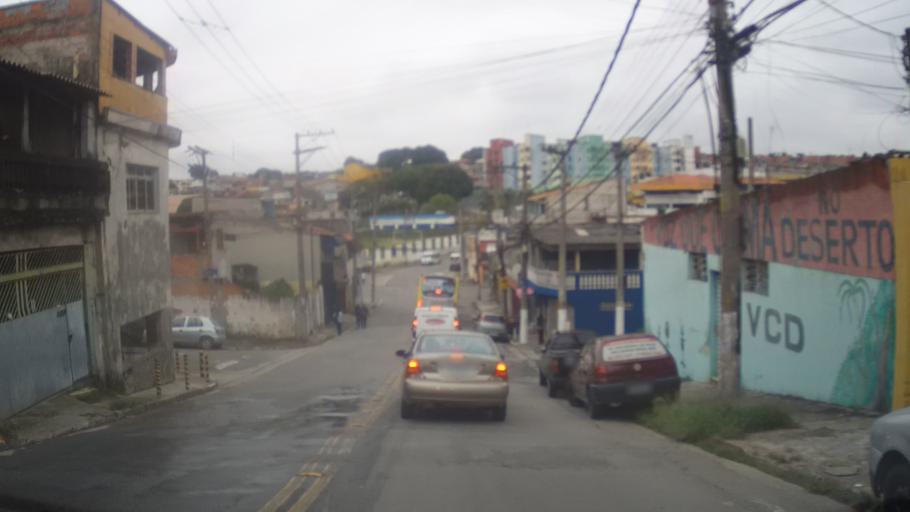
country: BR
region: Sao Paulo
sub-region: Guarulhos
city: Guarulhos
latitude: -23.4411
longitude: -46.5158
